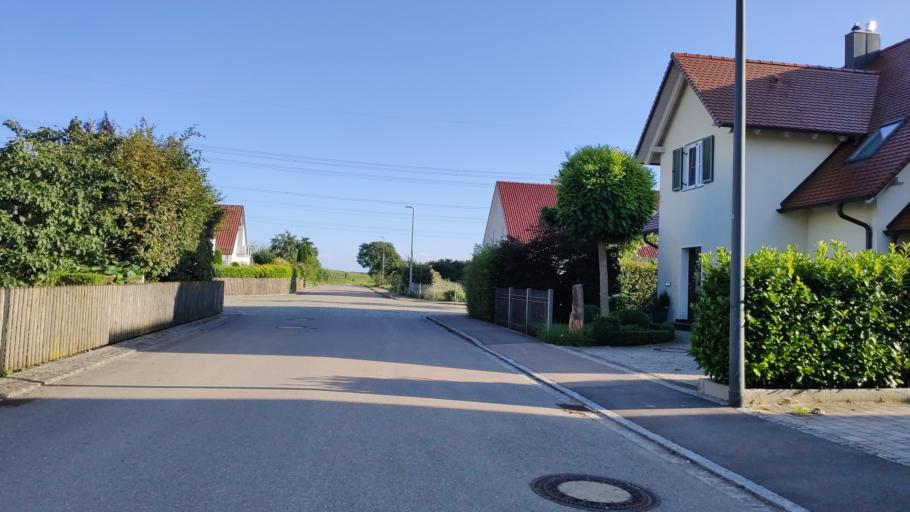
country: DE
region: Bavaria
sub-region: Swabia
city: Oberottmarshausen
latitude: 48.2334
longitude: 10.8582
